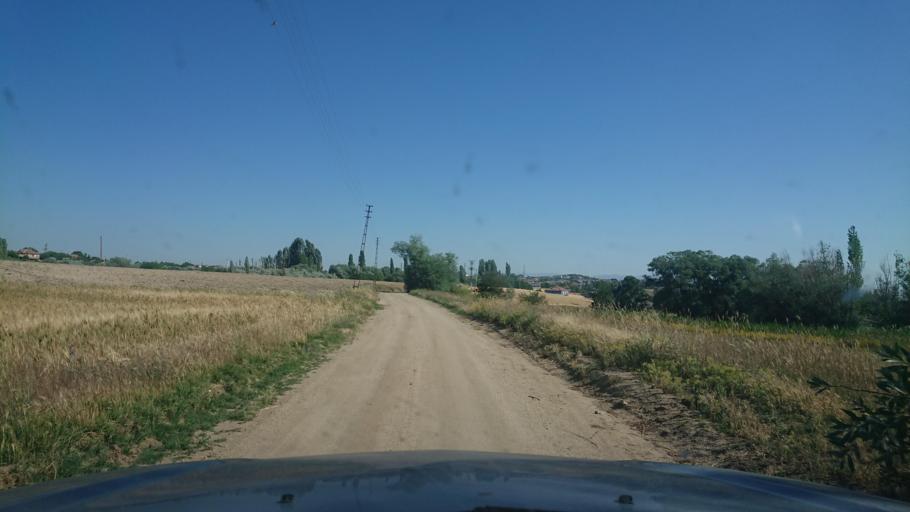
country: TR
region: Aksaray
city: Agacoren
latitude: 38.8584
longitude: 33.9122
